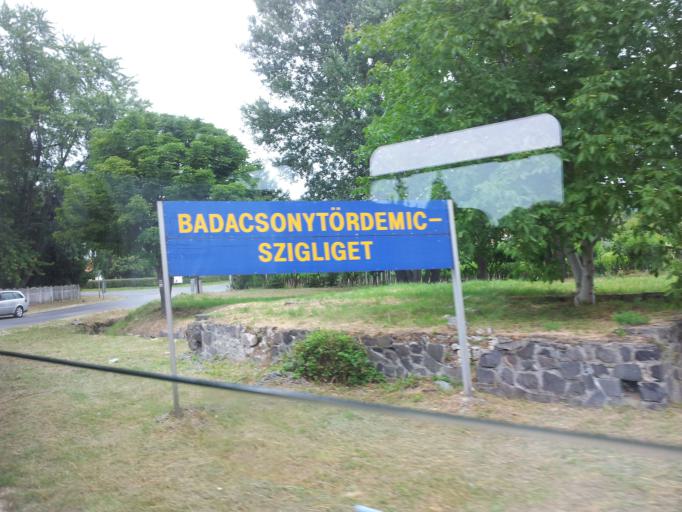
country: HU
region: Veszprem
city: Badacsonytomaj
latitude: 46.8081
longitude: 17.4687
